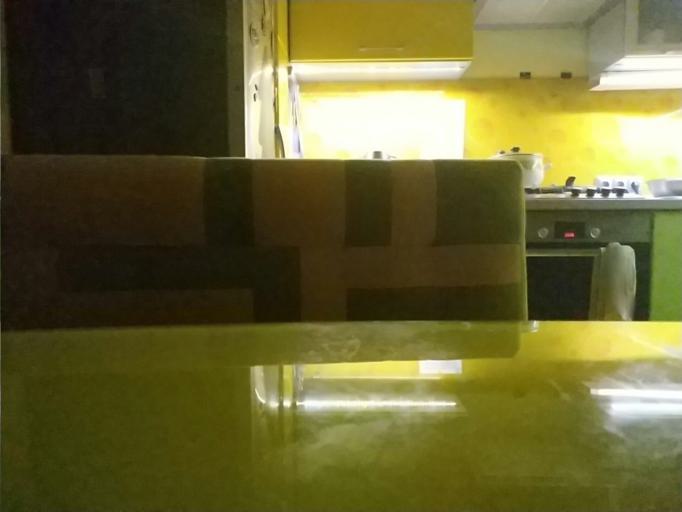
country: RU
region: Republic of Karelia
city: Pyaozerskiy
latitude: 65.8079
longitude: 30.4694
